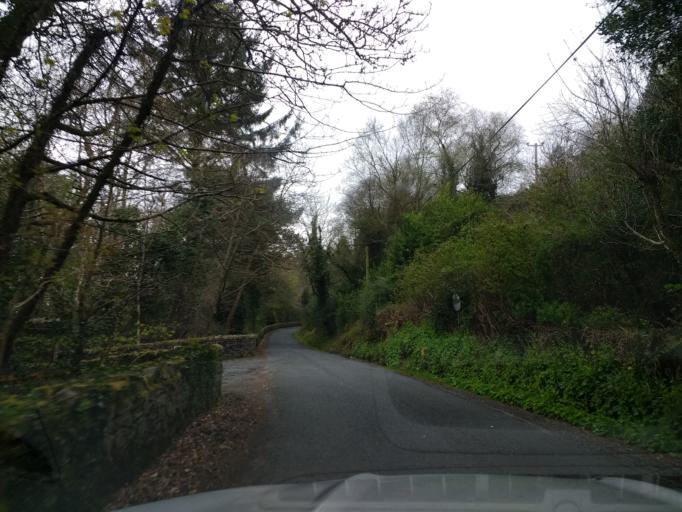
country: IE
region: Ulster
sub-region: County Donegal
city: Buncrana
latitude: 55.2197
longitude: -7.6118
